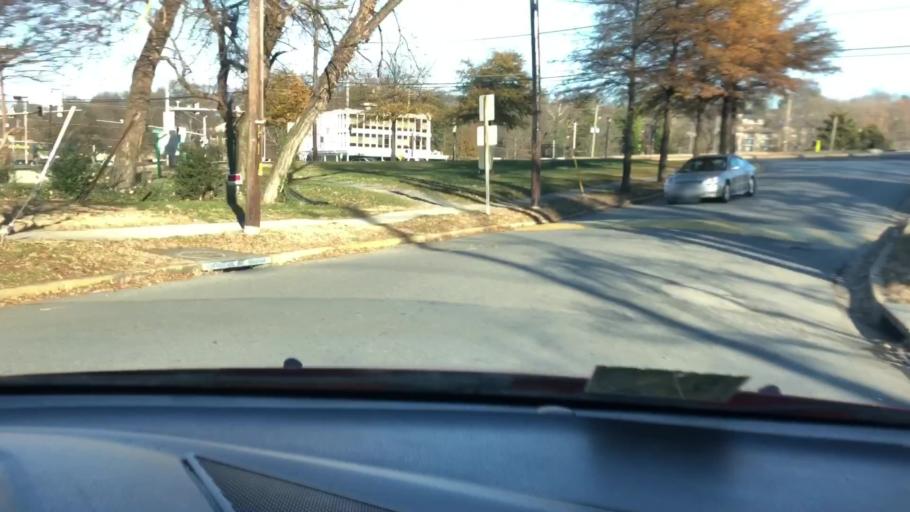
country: US
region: Maryland
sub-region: Prince George's County
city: Glassmanor
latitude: 38.8147
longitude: -76.9995
